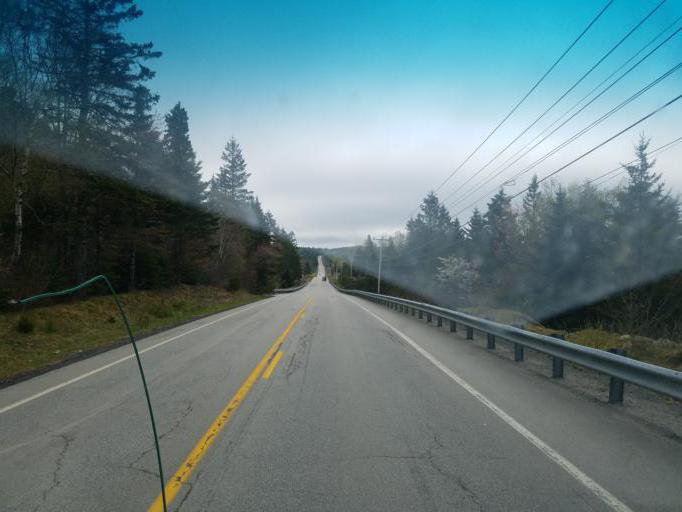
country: US
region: Maine
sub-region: Washington County
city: Eastport
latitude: 44.8010
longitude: -67.1241
